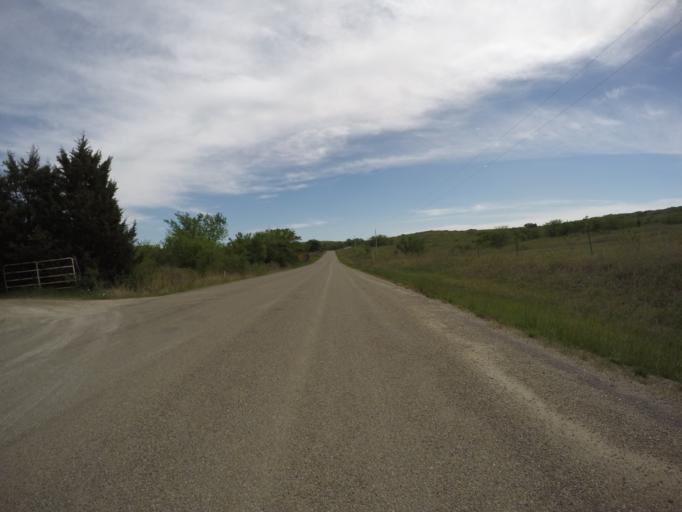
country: US
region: Kansas
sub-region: Riley County
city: Ogden
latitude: 39.0629
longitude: -96.6514
